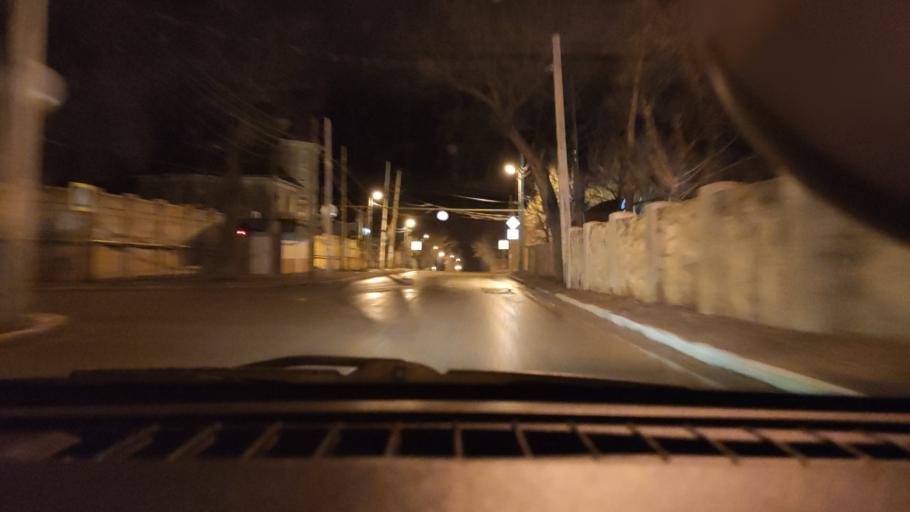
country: RU
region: Samara
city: Samara
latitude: 53.2755
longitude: 50.1913
